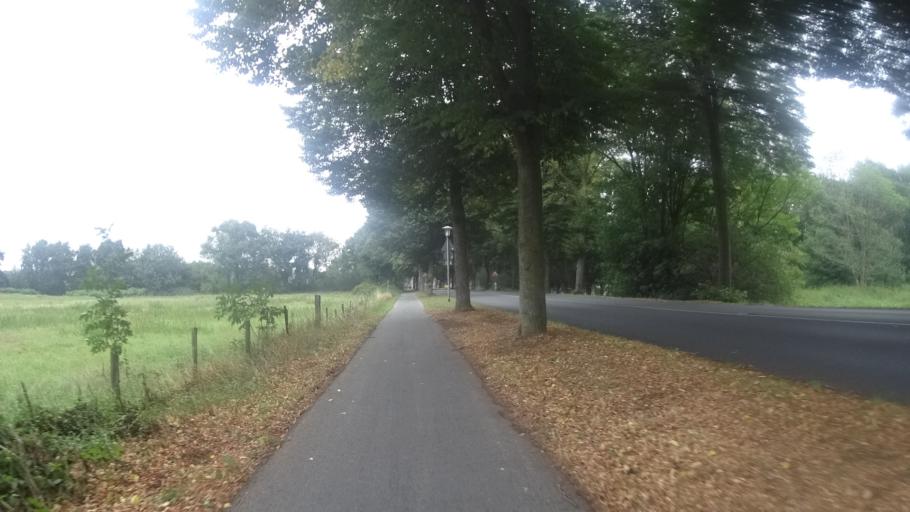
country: DE
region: North Rhine-Westphalia
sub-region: Regierungsbezirk Dusseldorf
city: Alpen
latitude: 51.5787
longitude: 6.5166
